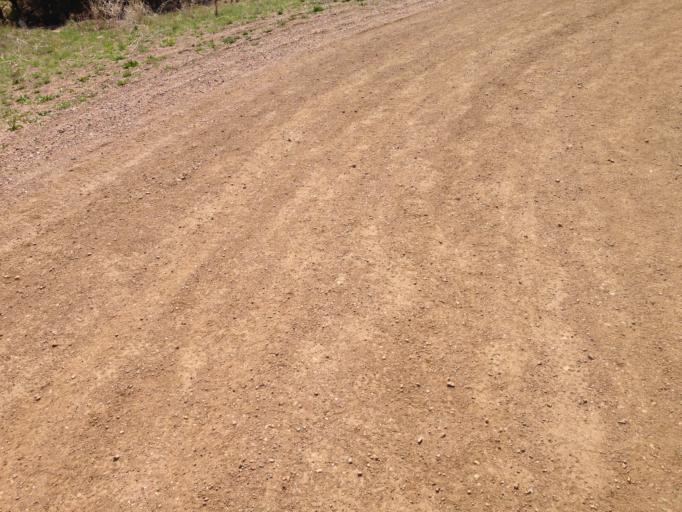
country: US
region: Colorado
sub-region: Boulder County
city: Boulder
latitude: 39.9268
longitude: -105.2728
